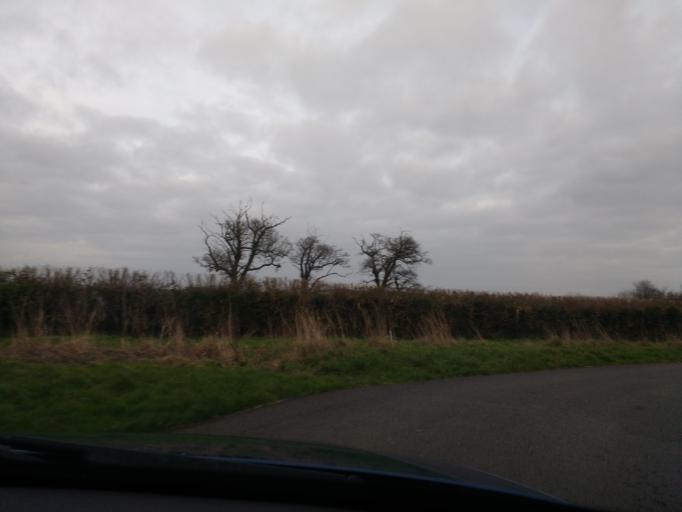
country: GB
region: England
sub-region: Isle of Wight
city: Shalfleet
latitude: 50.7145
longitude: -1.4007
